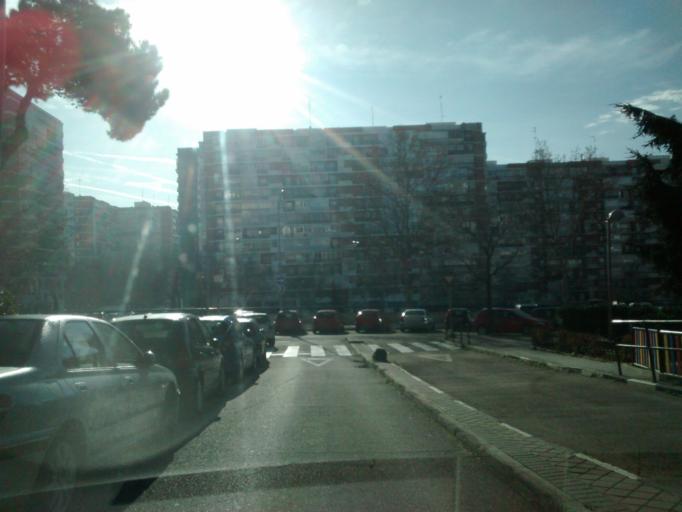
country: ES
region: Madrid
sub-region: Provincia de Madrid
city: Tetuan de las Victorias
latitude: 40.4802
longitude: -3.7152
